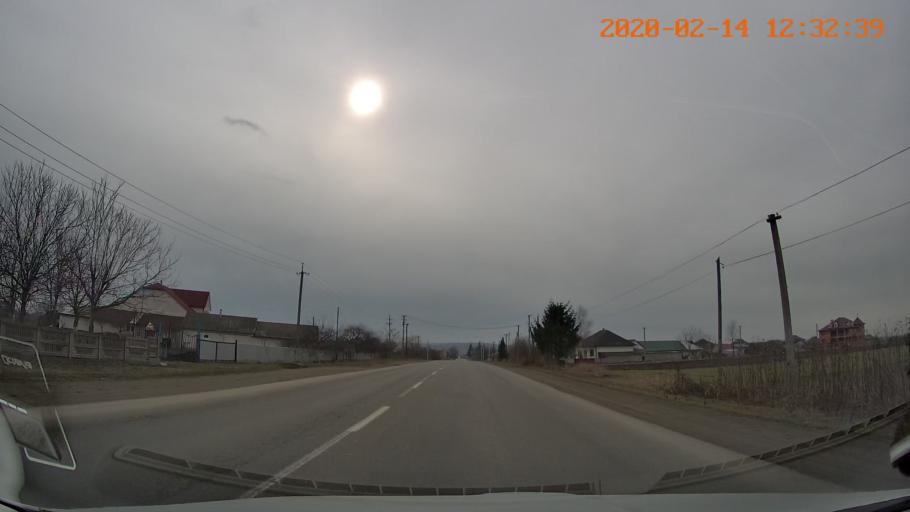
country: RO
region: Botosani
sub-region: Comuna Darabani
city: Bajura
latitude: 48.2411
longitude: 26.5481
